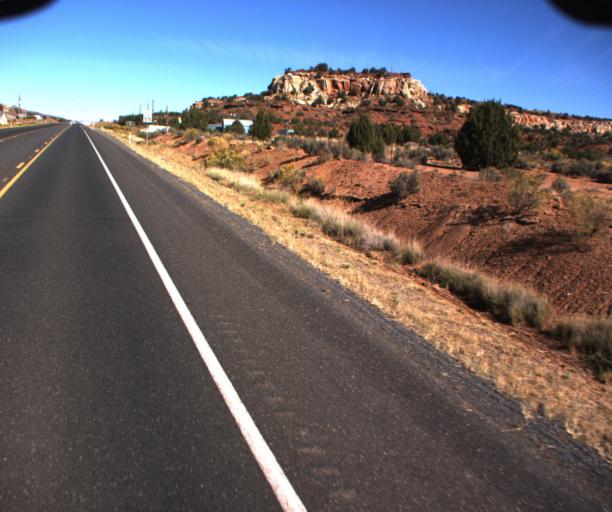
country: US
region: Arizona
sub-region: Coconino County
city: Fredonia
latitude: 36.9883
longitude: -112.5303
